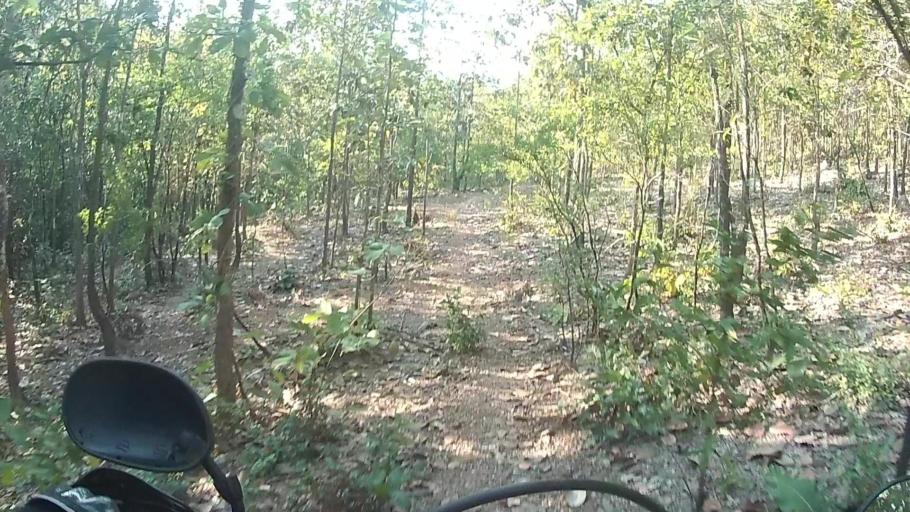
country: TH
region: Chiang Mai
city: San Sai
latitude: 18.9280
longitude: 99.1098
